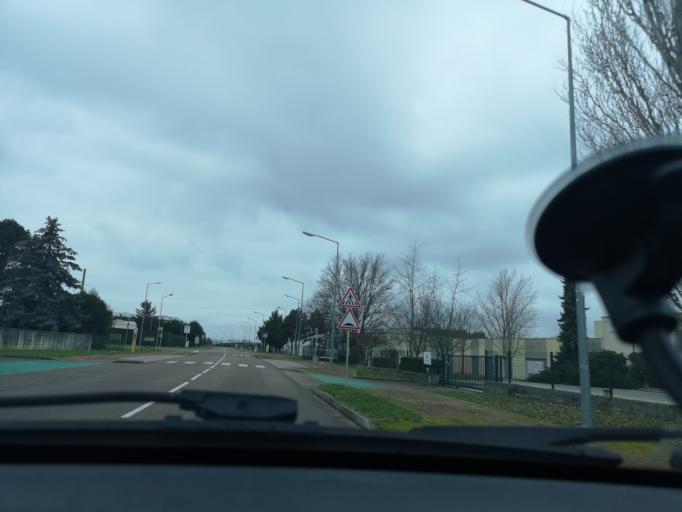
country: FR
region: Bourgogne
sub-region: Departement de Saone-et-Loire
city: Virey-le-Grand
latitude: 46.8225
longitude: 4.8691
